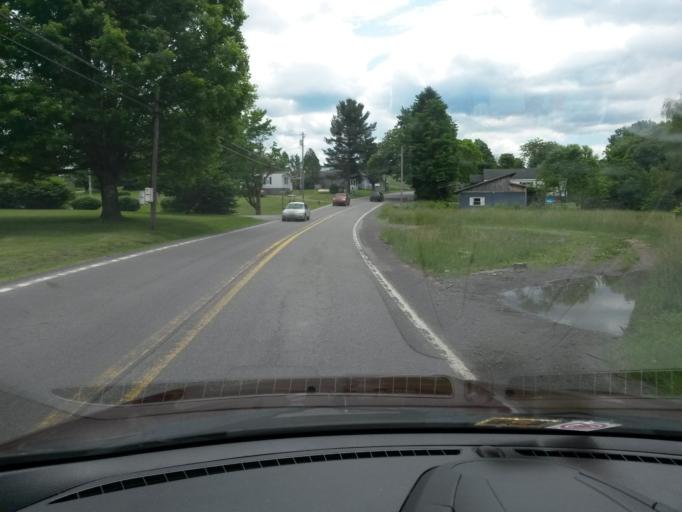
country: US
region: West Virginia
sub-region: Nicholas County
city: Craigsville
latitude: 38.2150
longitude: -80.6797
